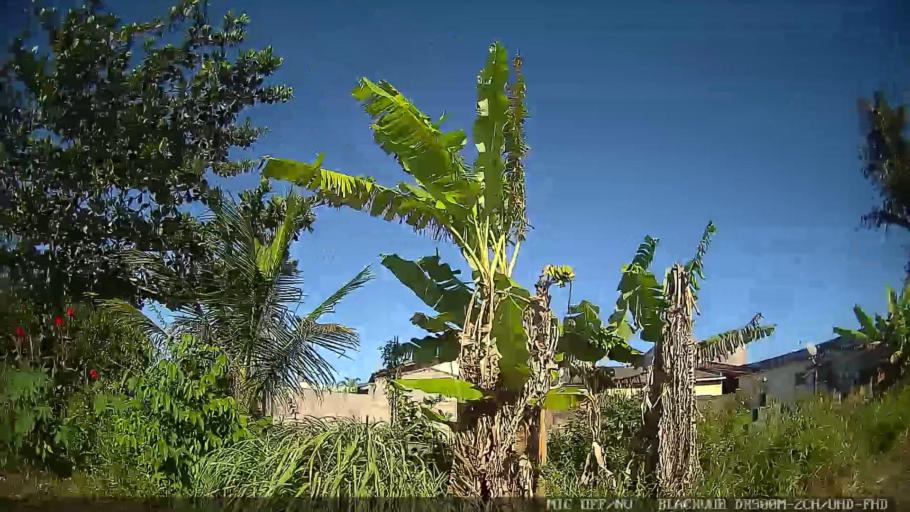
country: BR
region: Sao Paulo
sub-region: Itanhaem
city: Itanhaem
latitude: -24.2072
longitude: -46.8470
